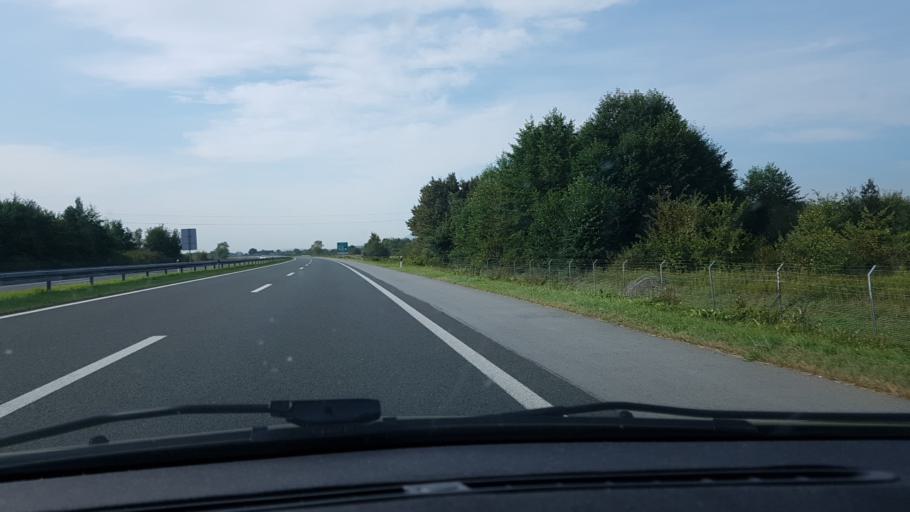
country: HR
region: Zagrebacka
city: Jakovlje
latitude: 45.9495
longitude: 15.8335
